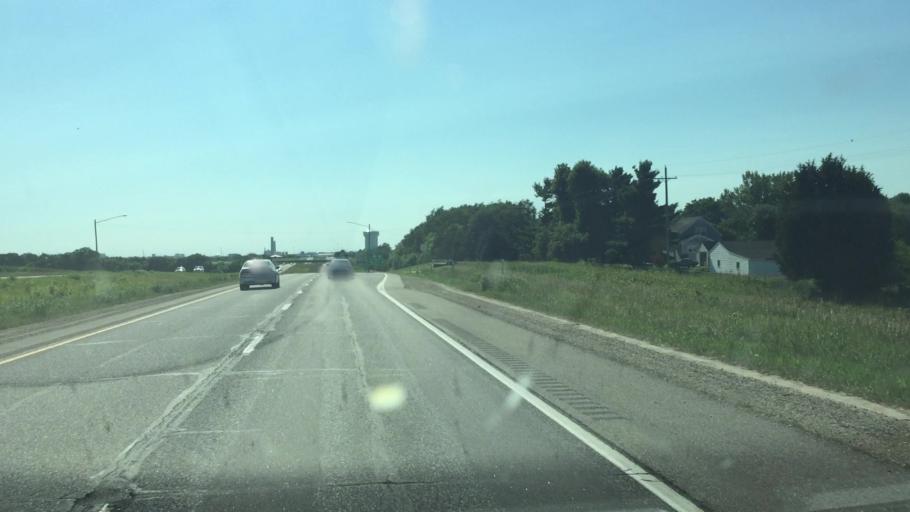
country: US
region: Iowa
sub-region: Linn County
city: Ely
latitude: 41.9267
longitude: -91.6223
